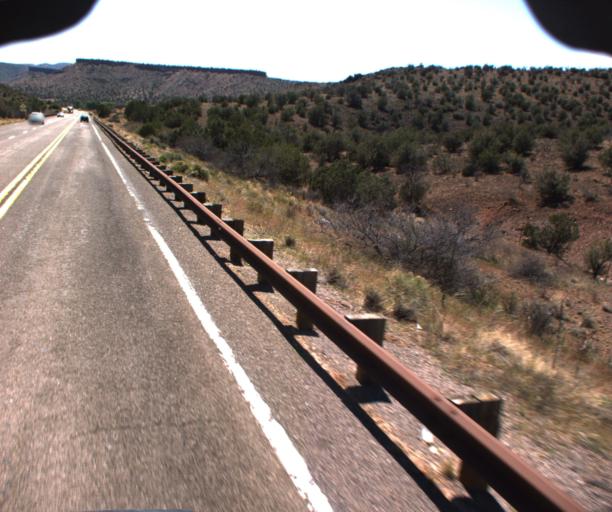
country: US
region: Arizona
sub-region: Mohave County
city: Peach Springs
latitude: 35.4469
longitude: -113.6380
